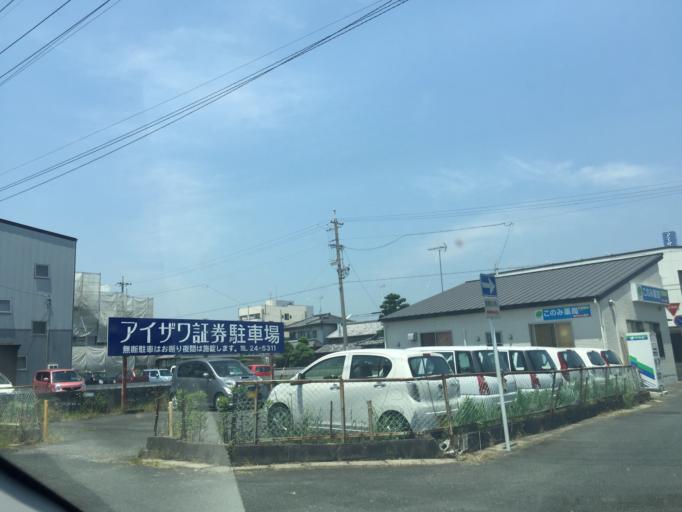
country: JP
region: Shizuoka
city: Kakegawa
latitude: 34.7694
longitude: 138.0123
